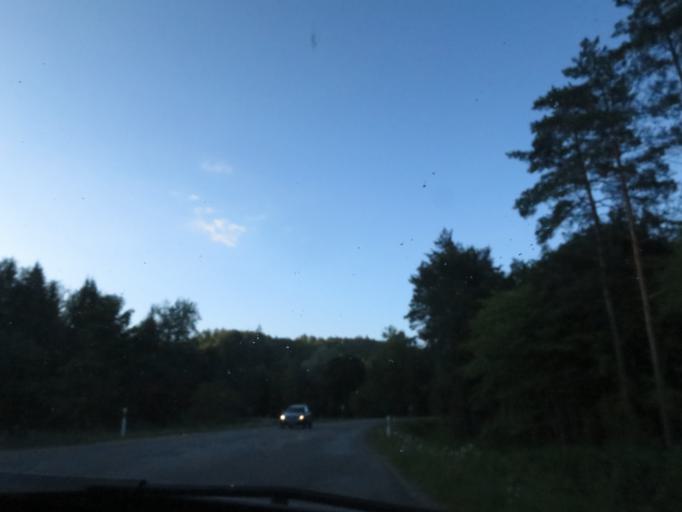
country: LV
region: Sigulda
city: Sigulda
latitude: 57.1698
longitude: 24.8379
